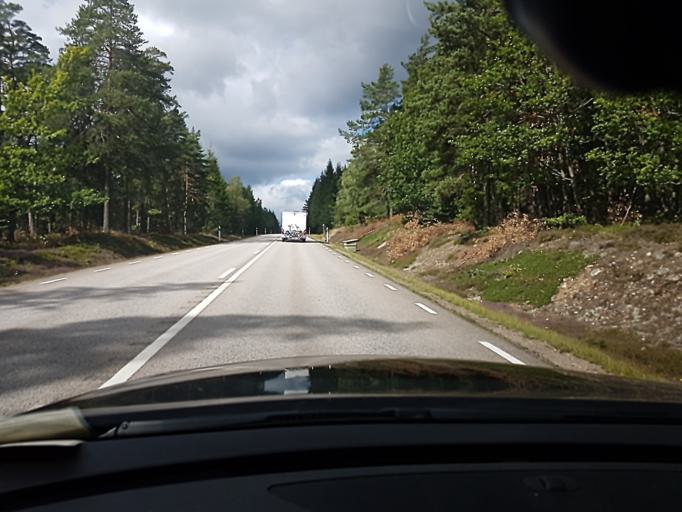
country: SE
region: Kronoberg
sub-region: Lessebo Kommun
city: Lessebo
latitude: 56.7298
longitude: 15.3603
